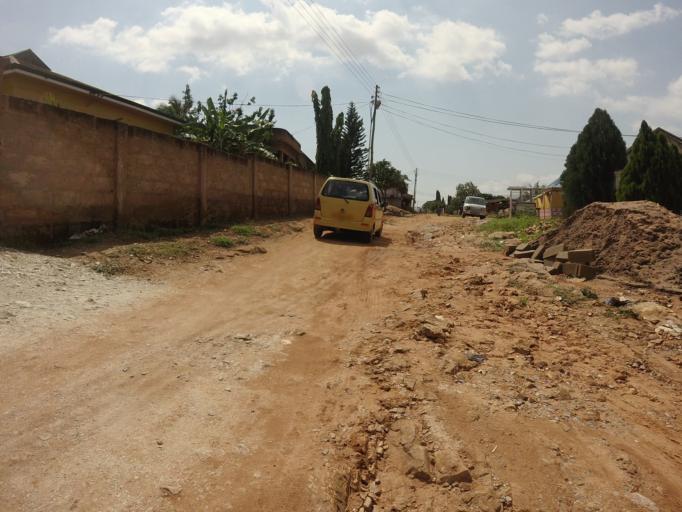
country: GH
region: Greater Accra
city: Gbawe
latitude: 5.6244
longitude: -0.3070
